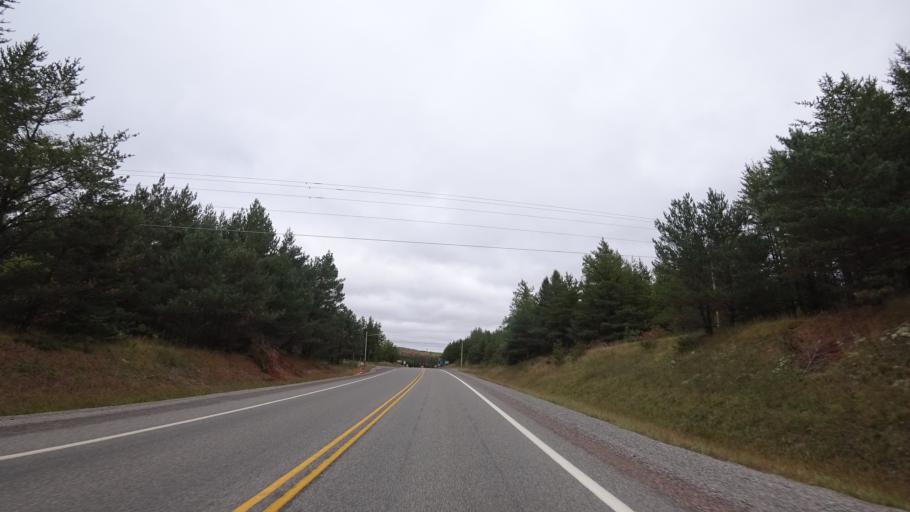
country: US
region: Michigan
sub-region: Marquette County
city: West Ishpeming
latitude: 46.4931
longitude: -87.9191
